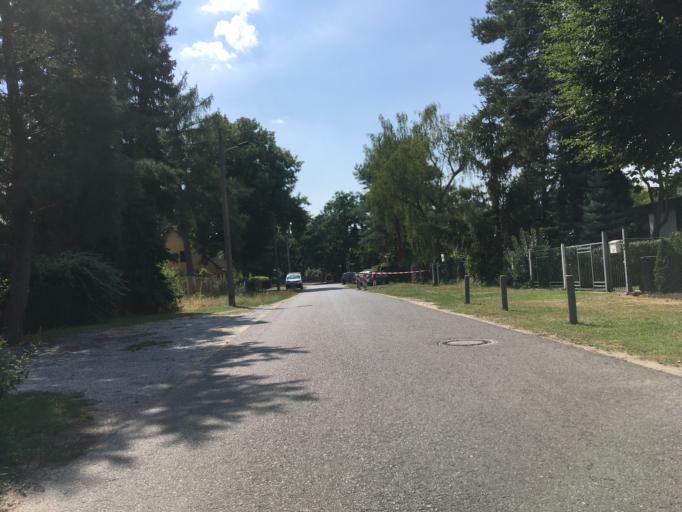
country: DE
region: Berlin
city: Mahlsdorf
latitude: 52.4845
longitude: 13.6114
